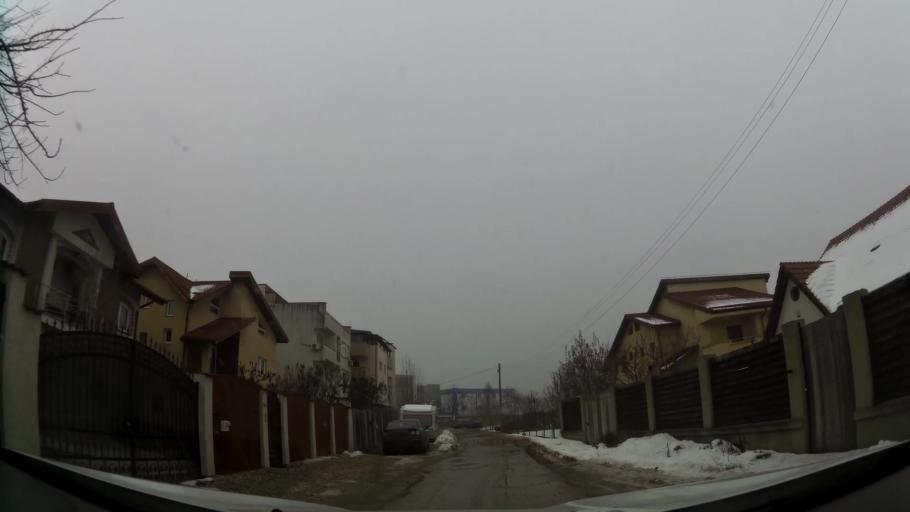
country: RO
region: Ilfov
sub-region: Comuna Chiajna
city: Rosu
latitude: 44.4387
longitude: 25.9981
